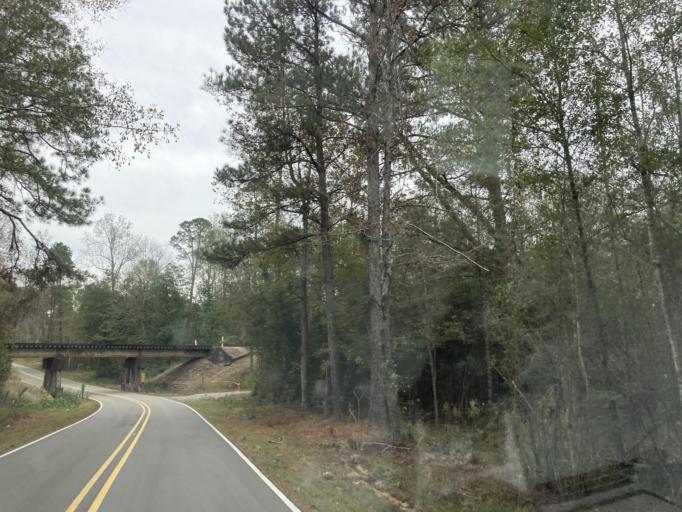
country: US
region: Mississippi
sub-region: Lamar County
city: Purvis
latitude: 31.1105
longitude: -89.4269
